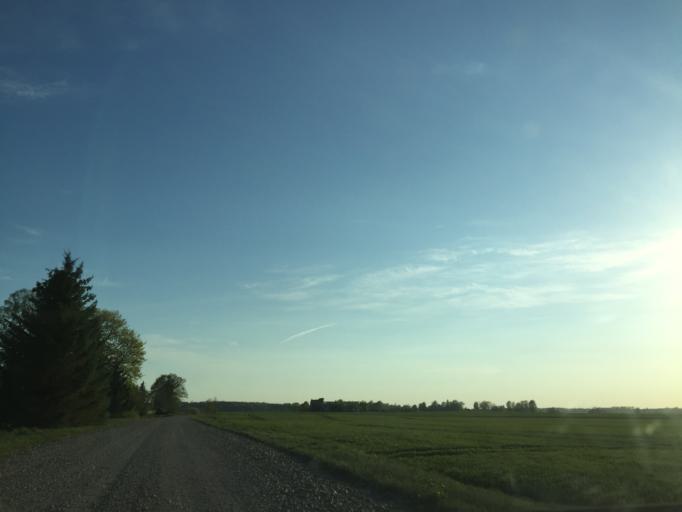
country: LV
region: Bauskas Rajons
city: Bauska
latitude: 56.2784
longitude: 24.2130
